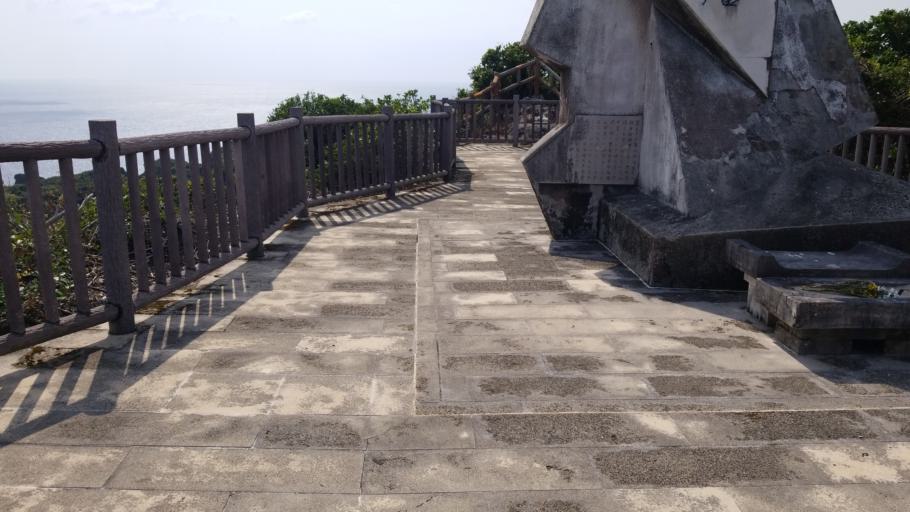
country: JP
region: Okinawa
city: Itoman
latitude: 26.0920
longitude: 127.7199
